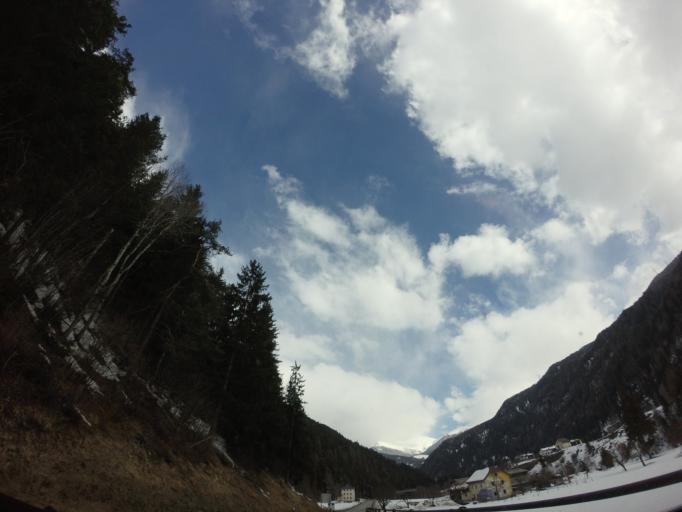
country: AT
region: Tyrol
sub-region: Politischer Bezirk Landeck
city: Nauders
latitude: 46.8668
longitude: 10.4406
